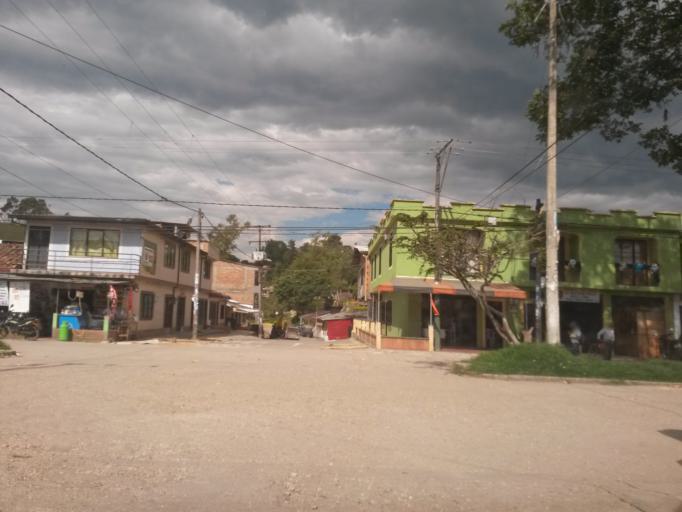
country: CO
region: Cauca
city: Rosas
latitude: 2.3546
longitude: -76.6859
